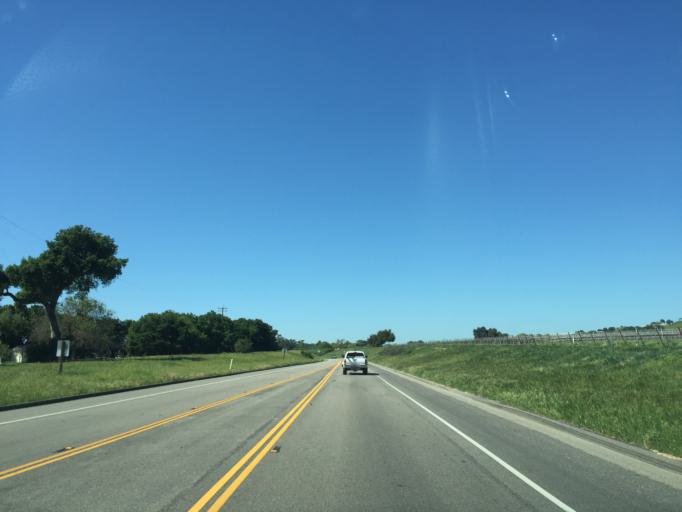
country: US
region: California
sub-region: Santa Barbara County
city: Los Olivos
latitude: 34.6586
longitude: -120.1022
